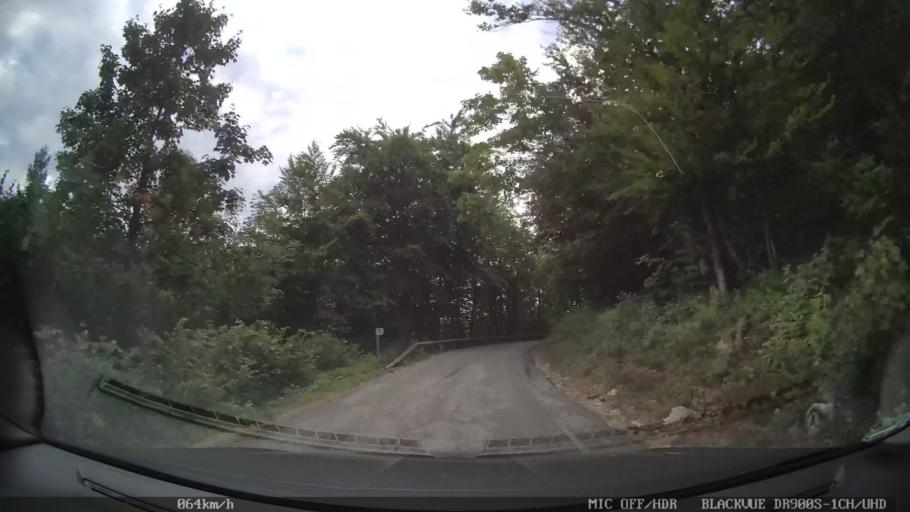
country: HR
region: Licko-Senjska
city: Jezerce
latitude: 44.9281
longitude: 15.5577
